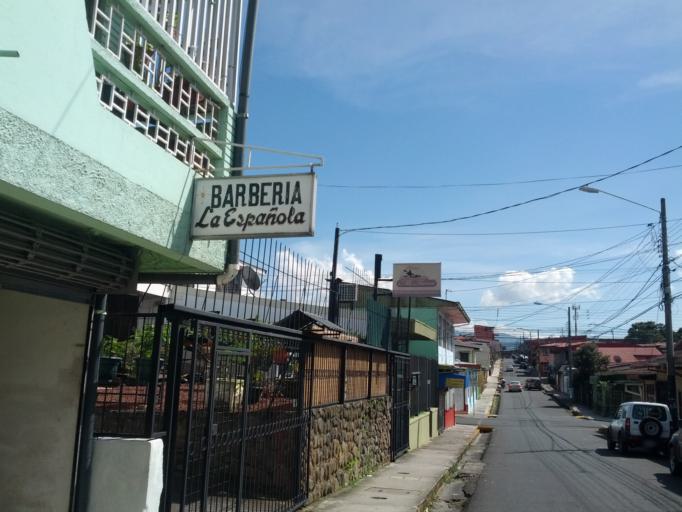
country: CR
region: Alajuela
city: Alajuela
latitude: 10.0159
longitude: -84.2110
